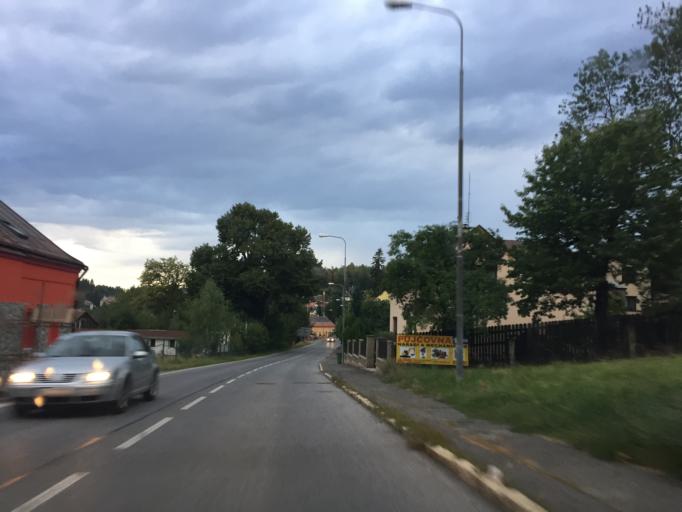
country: CZ
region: Liberecky
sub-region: Okres Jablonec nad Nisou
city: Jablonec nad Nisou
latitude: 50.7017
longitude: 15.1878
